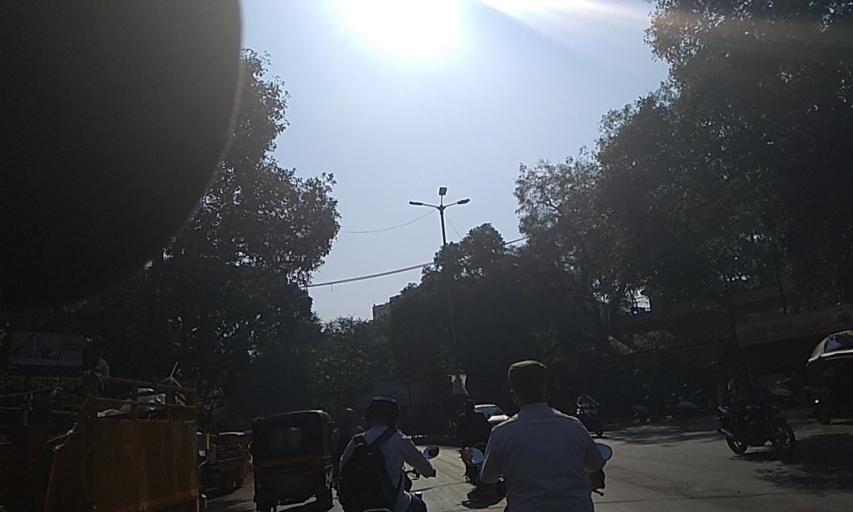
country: IN
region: Maharashtra
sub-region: Pune Division
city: Pune
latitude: 18.4993
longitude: 73.8508
